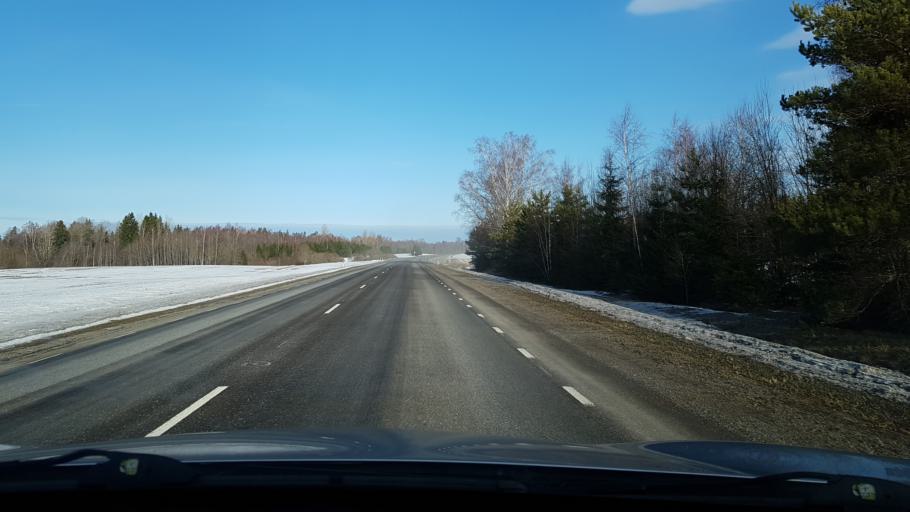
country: EE
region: Viljandimaa
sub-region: Viljandi linn
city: Viljandi
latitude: 58.4288
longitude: 25.5963
